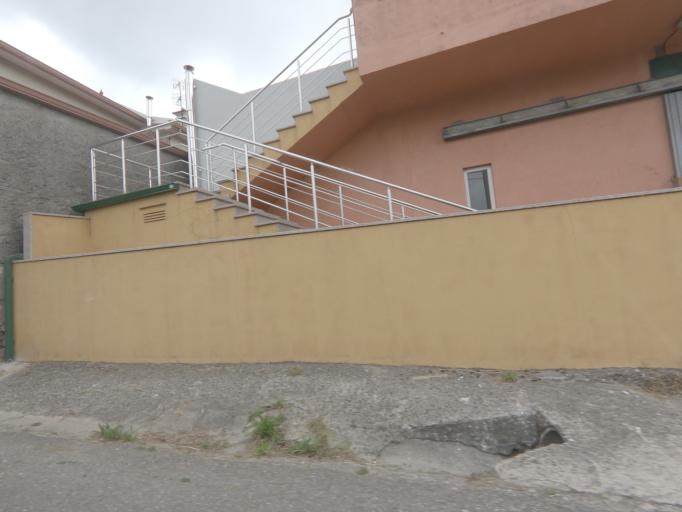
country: ES
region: Galicia
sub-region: Provincia de Pontevedra
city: Tui
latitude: 42.0483
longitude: -8.6580
